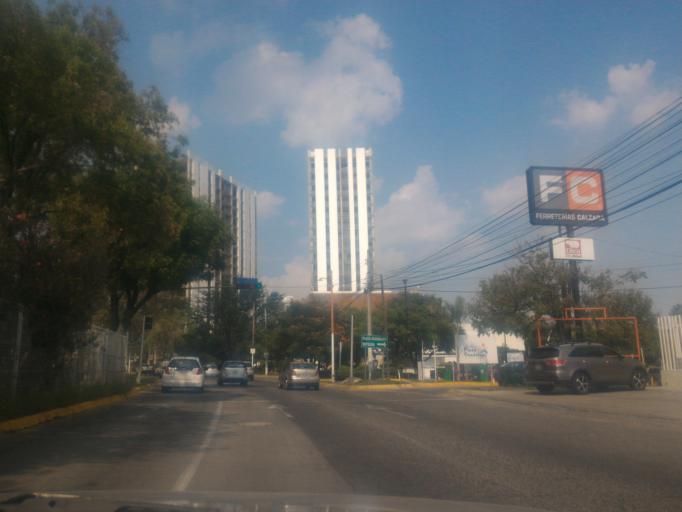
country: MX
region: Jalisco
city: Guadalajara
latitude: 20.6586
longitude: -103.4334
